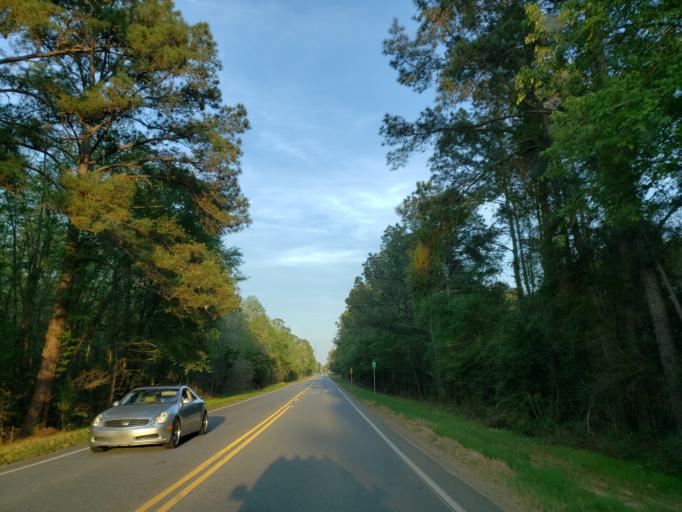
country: US
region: Georgia
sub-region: Lowndes County
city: Hahira
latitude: 30.9950
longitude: -83.4086
